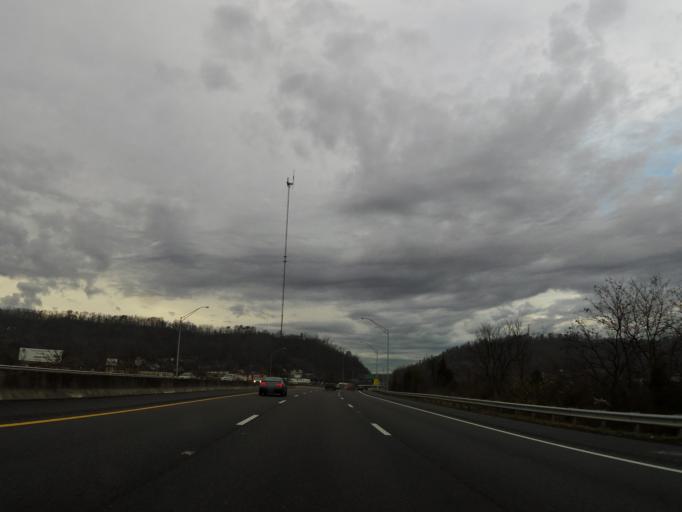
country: US
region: Tennessee
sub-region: Knox County
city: Knoxville
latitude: 35.9862
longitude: -83.9489
